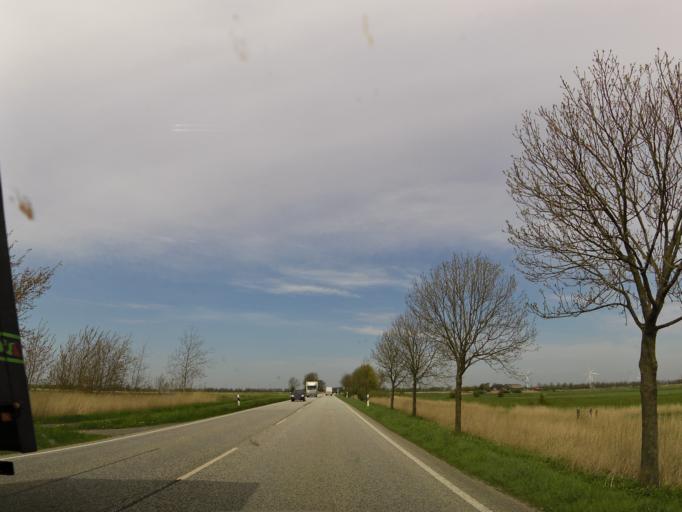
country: DE
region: Schleswig-Holstein
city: Husum
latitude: 54.4339
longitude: 9.0483
